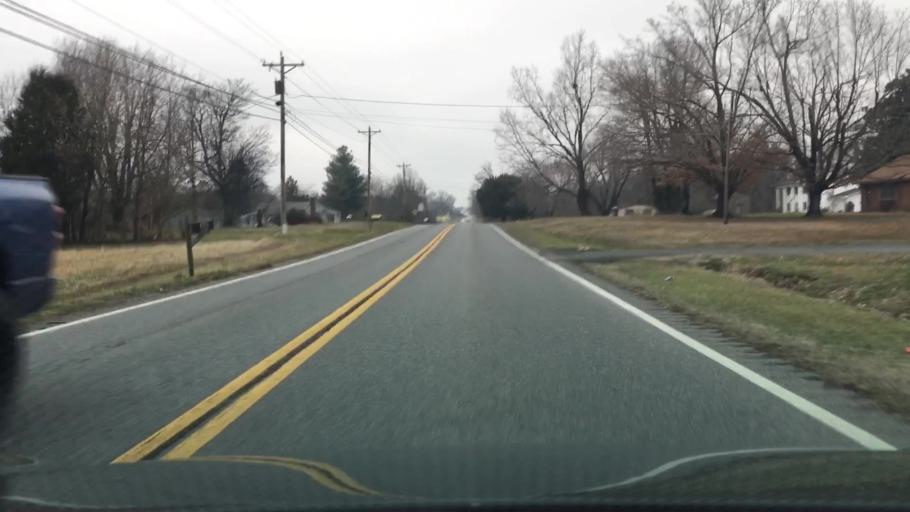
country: US
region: Kentucky
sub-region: McCracken County
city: Reidland
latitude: 36.9847
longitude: -88.4940
